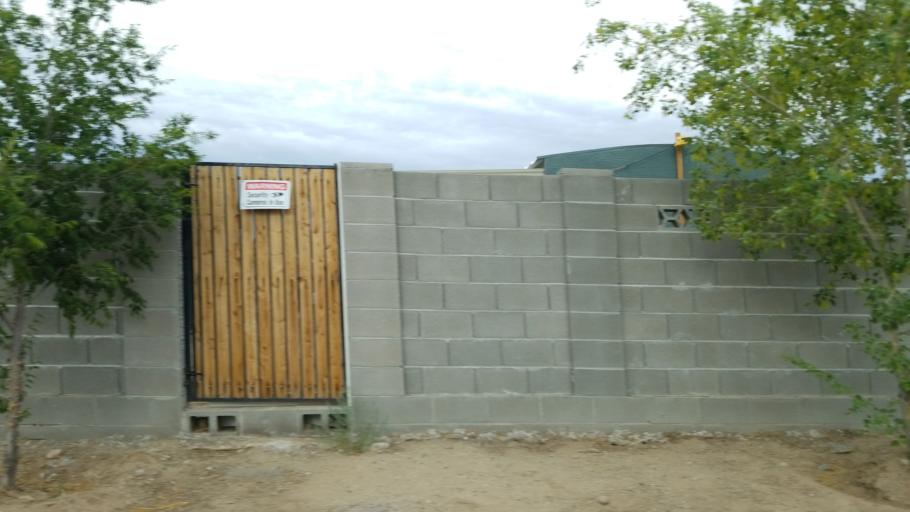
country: US
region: Arizona
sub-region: Maricopa County
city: Laveen
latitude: 33.3597
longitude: -112.0919
